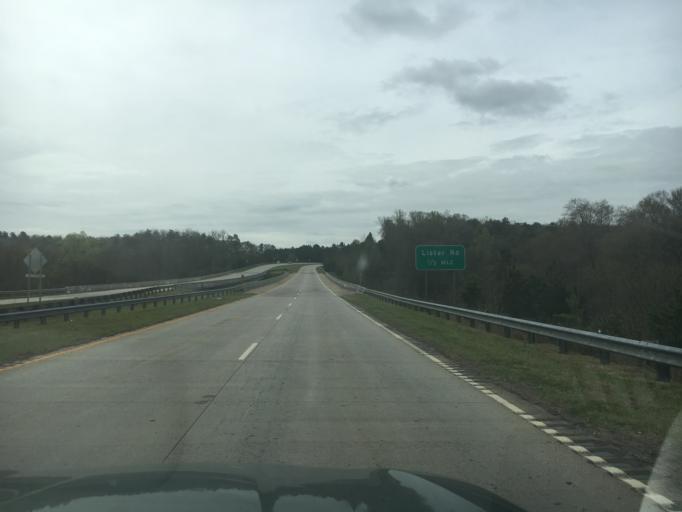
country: US
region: South Carolina
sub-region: Spartanburg County
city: Duncan
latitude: 34.9508
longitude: -82.1799
